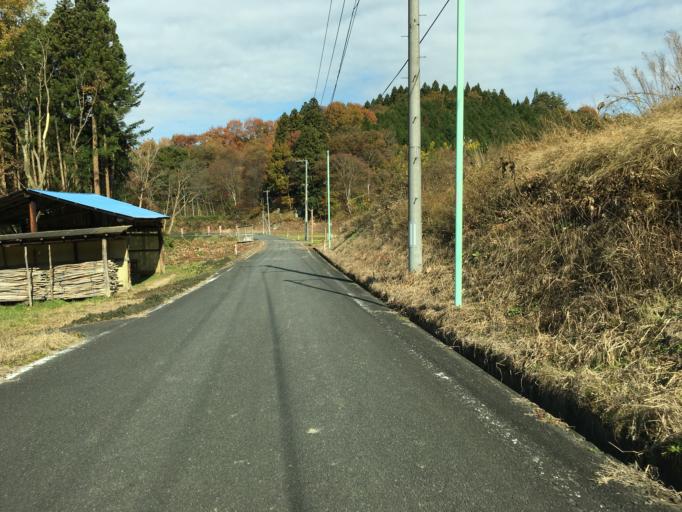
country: JP
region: Fukushima
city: Ishikawa
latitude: 37.1673
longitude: 140.5567
